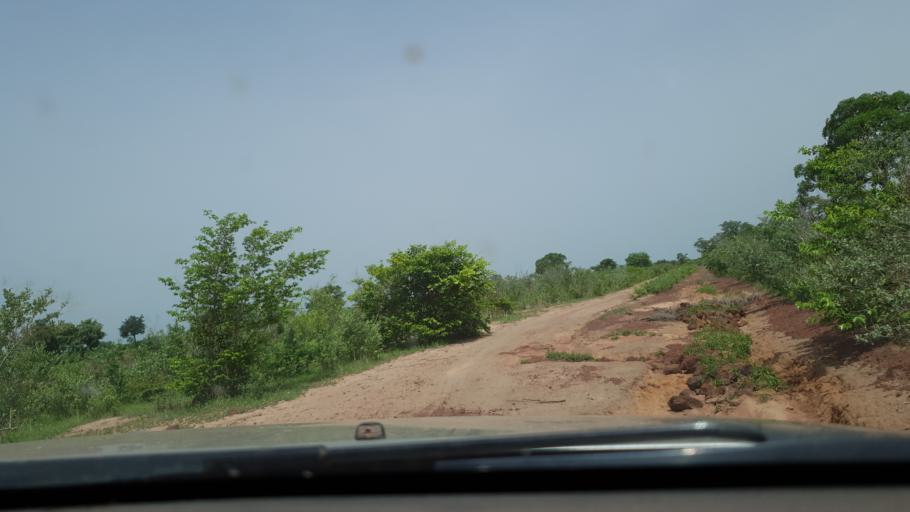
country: ML
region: Koulikoro
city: Koulikoro
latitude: 12.6648
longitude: -7.2187
